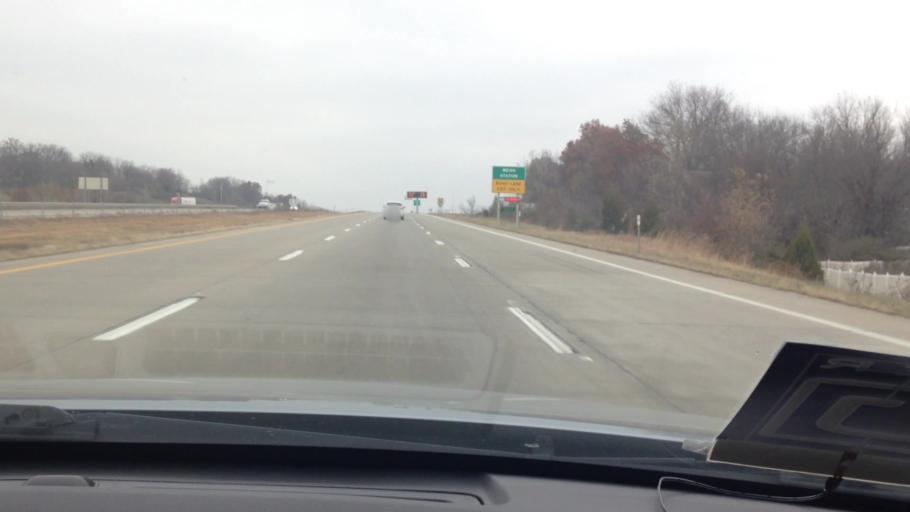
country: US
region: Missouri
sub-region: Cass County
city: Harrisonville
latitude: 38.6239
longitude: -94.3493
